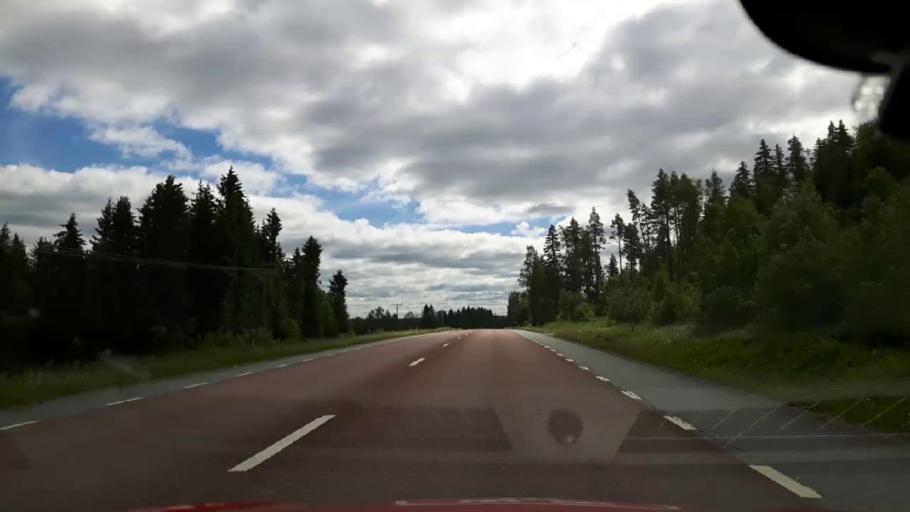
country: SE
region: Jaemtland
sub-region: Braecke Kommun
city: Braecke
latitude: 62.9360
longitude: 15.2036
